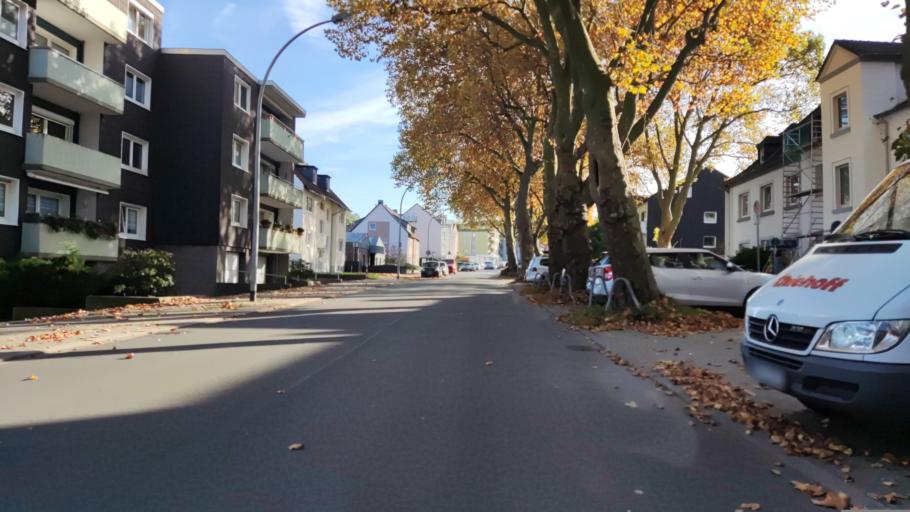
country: DE
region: North Rhine-Westphalia
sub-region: Regierungsbezirk Arnsberg
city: Herne
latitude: 51.5218
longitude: 7.2266
